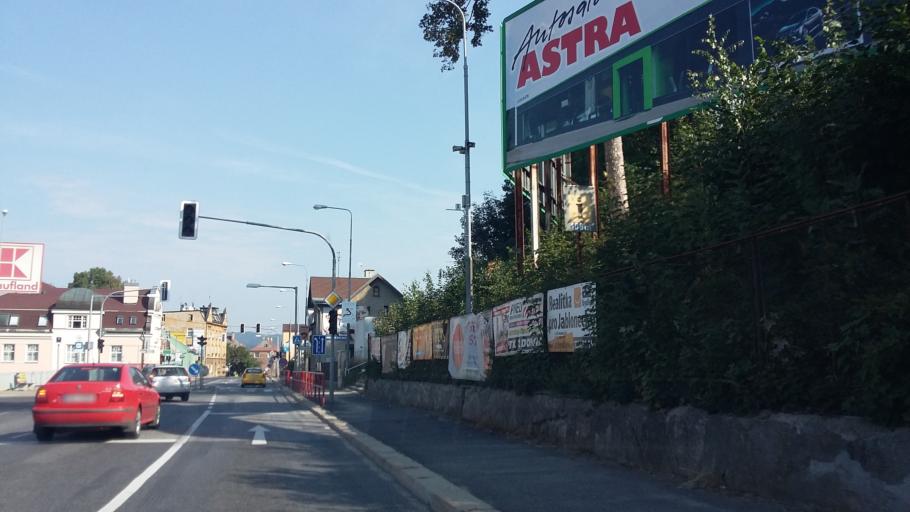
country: CZ
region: Liberecky
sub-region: Okres Jablonec nad Nisou
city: Jablonec nad Nisou
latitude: 50.7153
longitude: 15.1611
